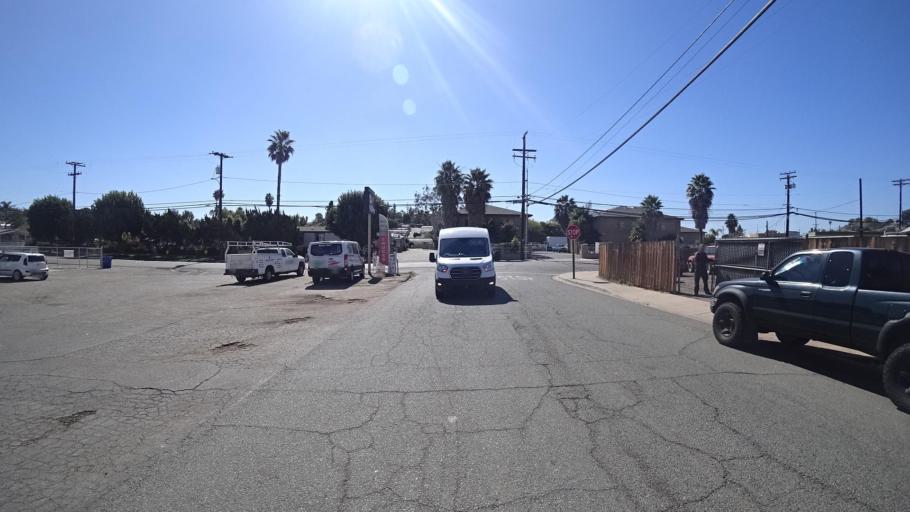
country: US
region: California
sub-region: San Diego County
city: Winter Gardens
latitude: 32.8211
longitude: -116.9335
